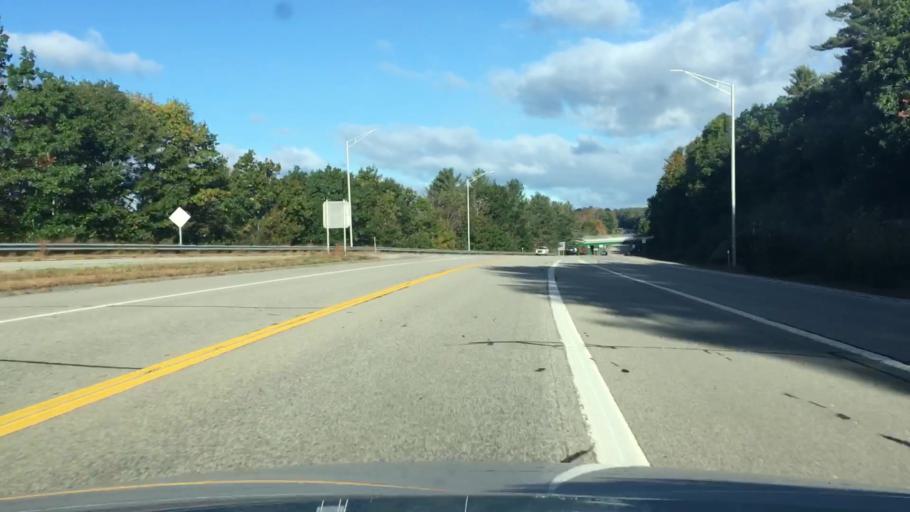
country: US
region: New Hampshire
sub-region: Strafford County
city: Durham
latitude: 43.1402
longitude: -70.9140
